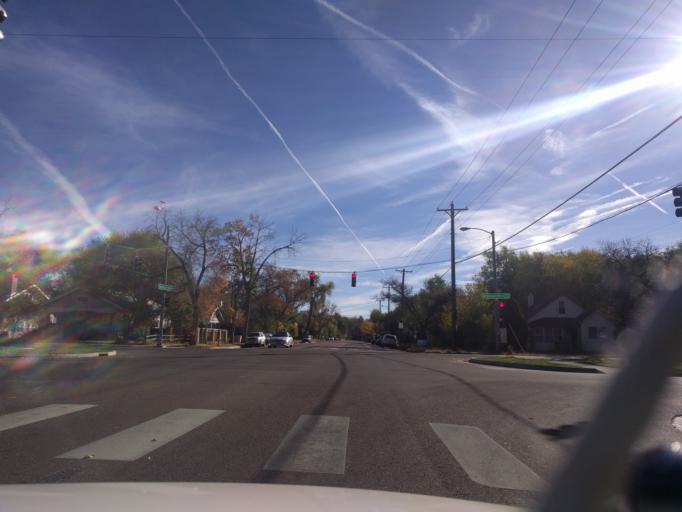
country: US
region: Colorado
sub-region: El Paso County
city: Colorado Springs
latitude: 38.8463
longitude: -104.8177
